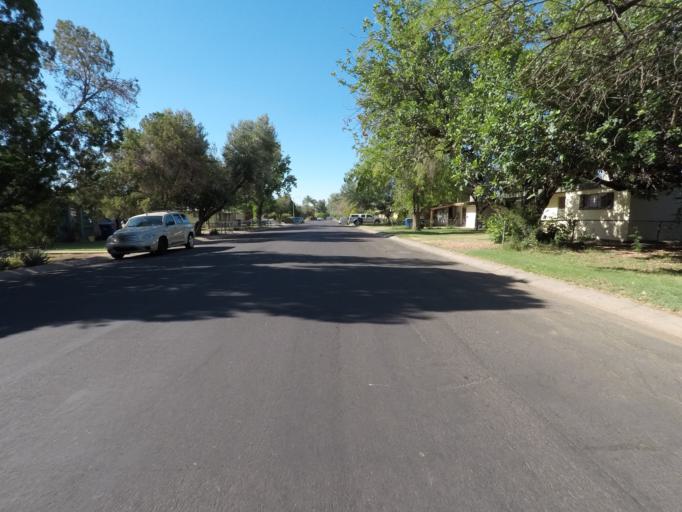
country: US
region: Arizona
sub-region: Maricopa County
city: Tempe Junction
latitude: 33.4121
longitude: -111.9443
